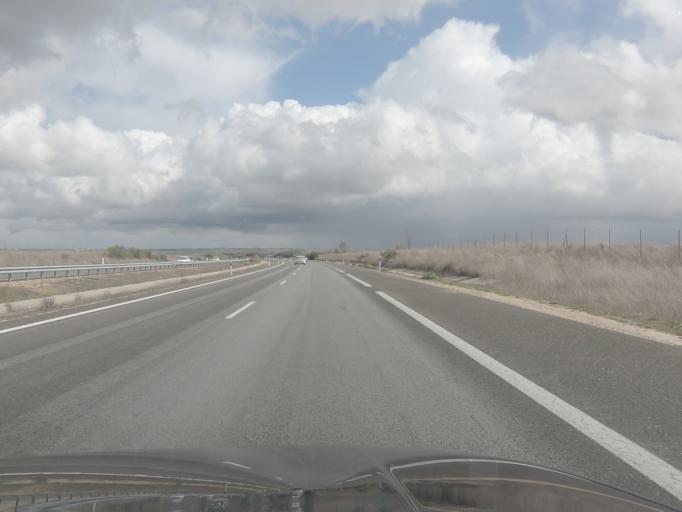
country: ES
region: Castille and Leon
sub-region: Provincia de Salamanca
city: Castellanos de Villiquera
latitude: 41.0588
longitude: -5.6805
